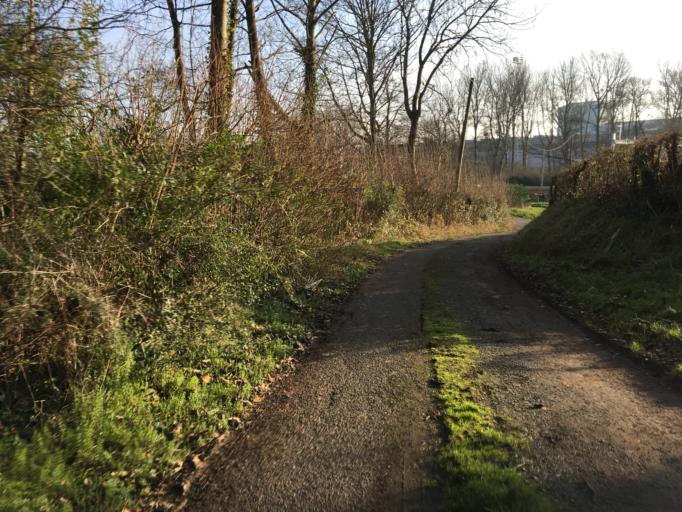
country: GB
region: Wales
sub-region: Newport
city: Bishton
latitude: 51.5812
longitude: -2.8863
